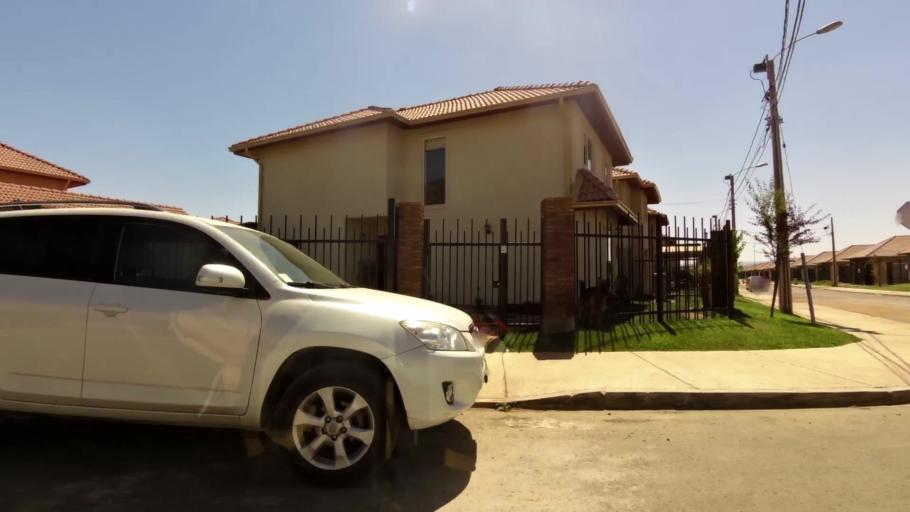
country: CL
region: Maule
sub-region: Provincia de Talca
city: Talca
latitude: -35.4341
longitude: -71.5919
